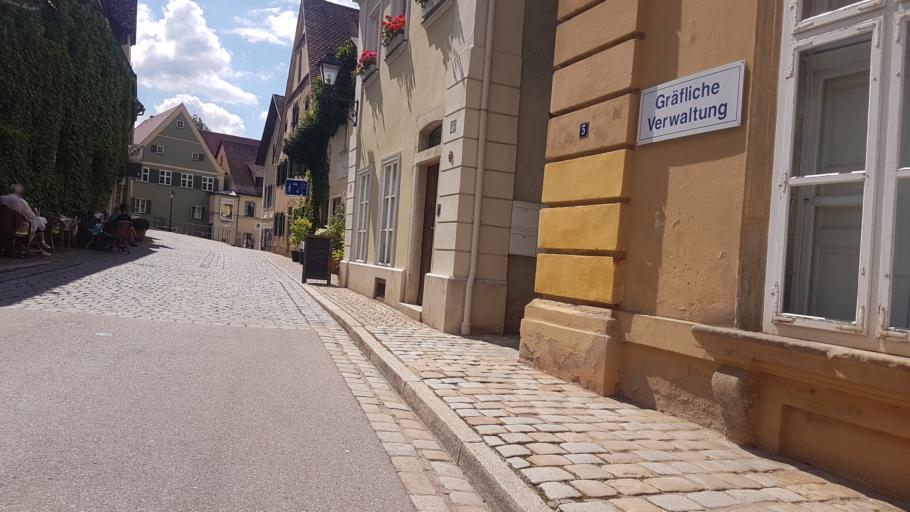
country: DE
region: Bavaria
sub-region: Regierungsbezirk Mittelfranken
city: Pappenheim
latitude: 48.9347
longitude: 10.9740
